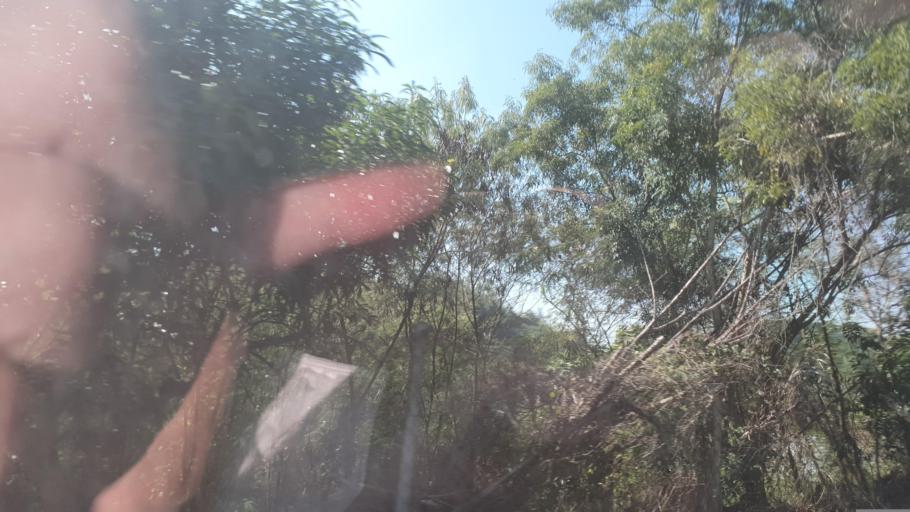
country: TW
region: Taiwan
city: Yujing
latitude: 23.0509
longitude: 120.3820
